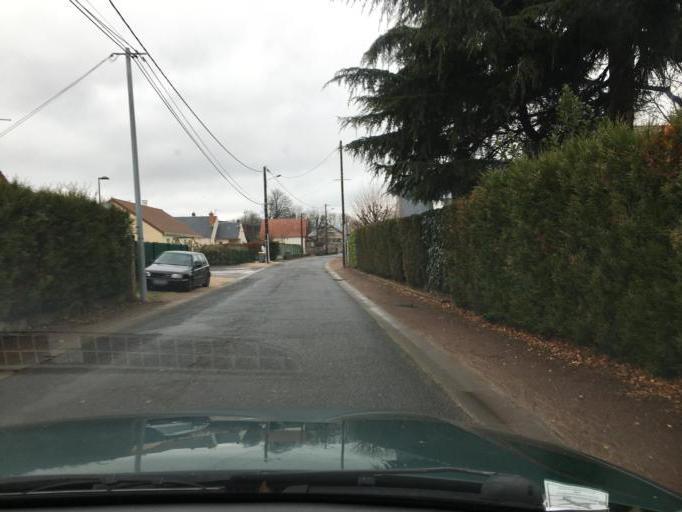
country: FR
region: Centre
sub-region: Departement du Loiret
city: Saint-Pryve-Saint-Mesmin
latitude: 47.8665
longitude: 1.8766
